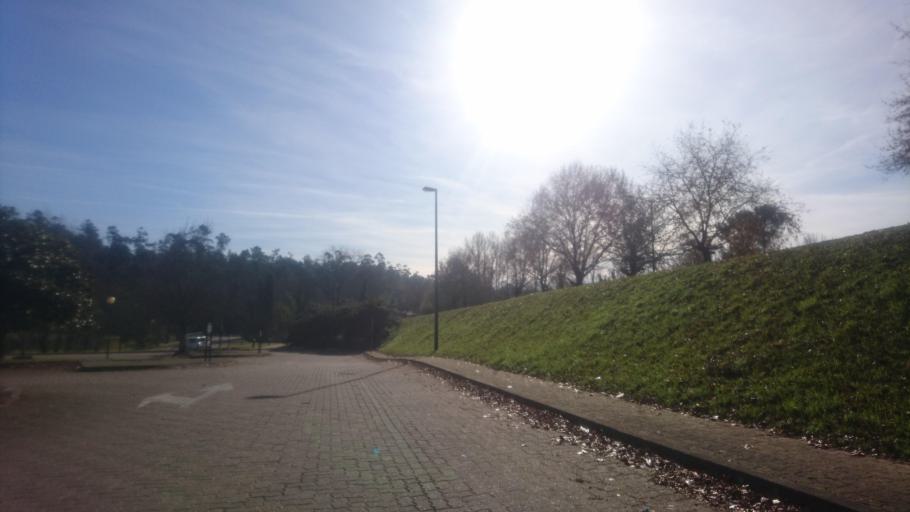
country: PT
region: Aveiro
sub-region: Santa Maria da Feira
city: Rio Meao
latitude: 40.9328
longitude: -8.5776
